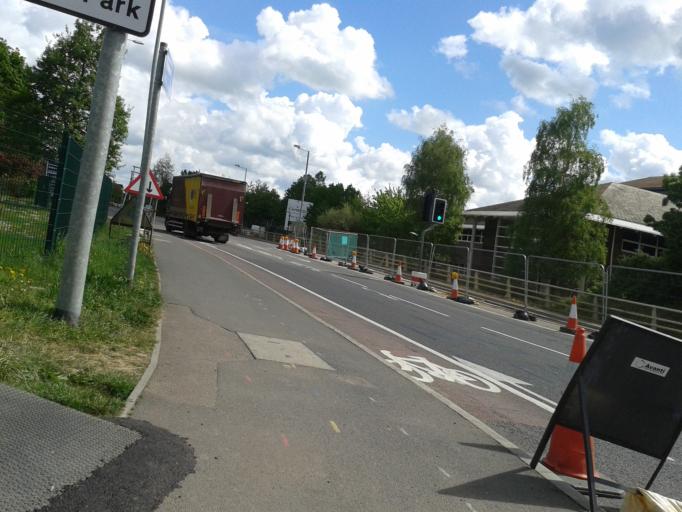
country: GB
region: England
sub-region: Cambridgeshire
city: Cambridge
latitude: 52.2297
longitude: 0.1484
